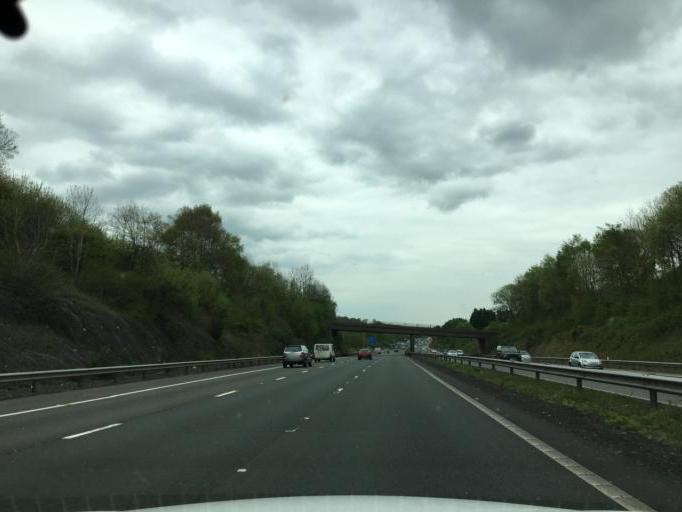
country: GB
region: Wales
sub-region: Caerphilly County Borough
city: Caerphilly
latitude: 51.5461
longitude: -3.1926
